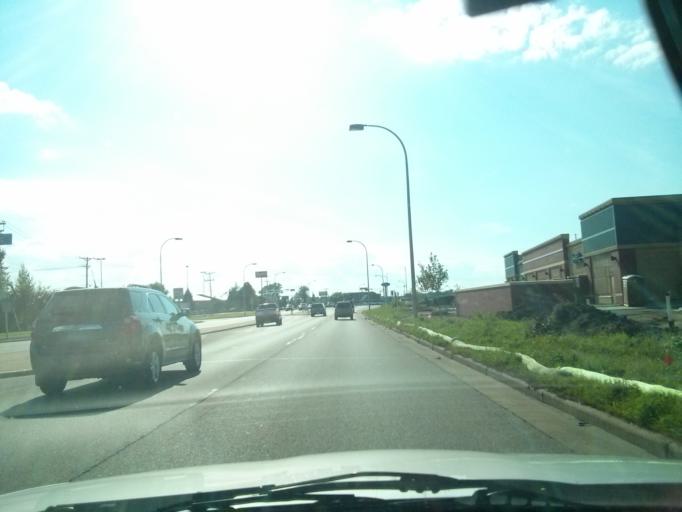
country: US
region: Wisconsin
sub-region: Saint Croix County
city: Hudson
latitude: 44.9611
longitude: -92.7249
